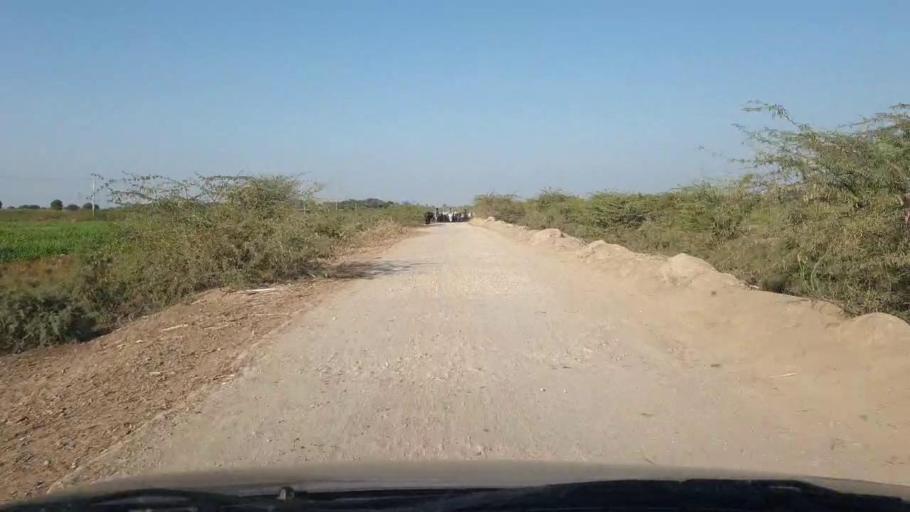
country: PK
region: Sindh
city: Samaro
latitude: 25.1543
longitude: 69.3110
